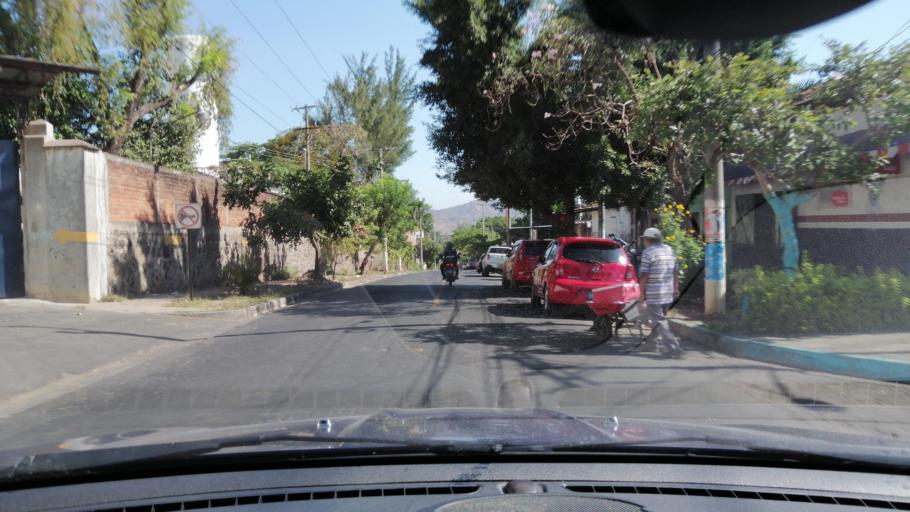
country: SV
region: Santa Ana
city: Santa Ana
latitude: 13.9911
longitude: -89.5505
